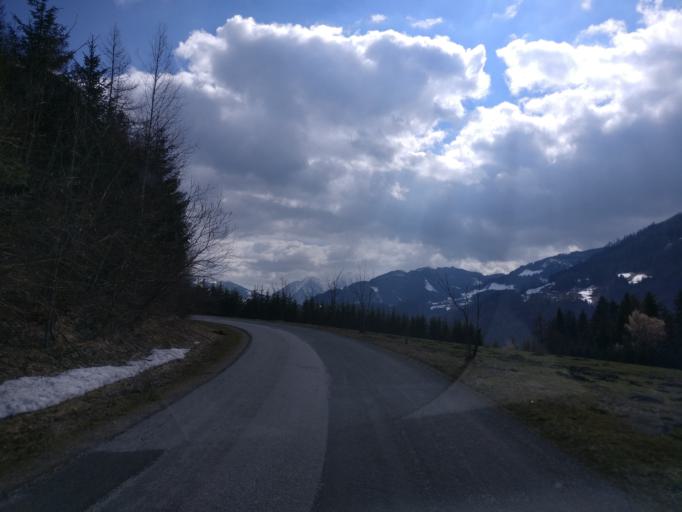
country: AT
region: Salzburg
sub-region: Politischer Bezirk Sankt Johann im Pongau
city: Bischofshofen
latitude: 47.4390
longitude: 13.2209
